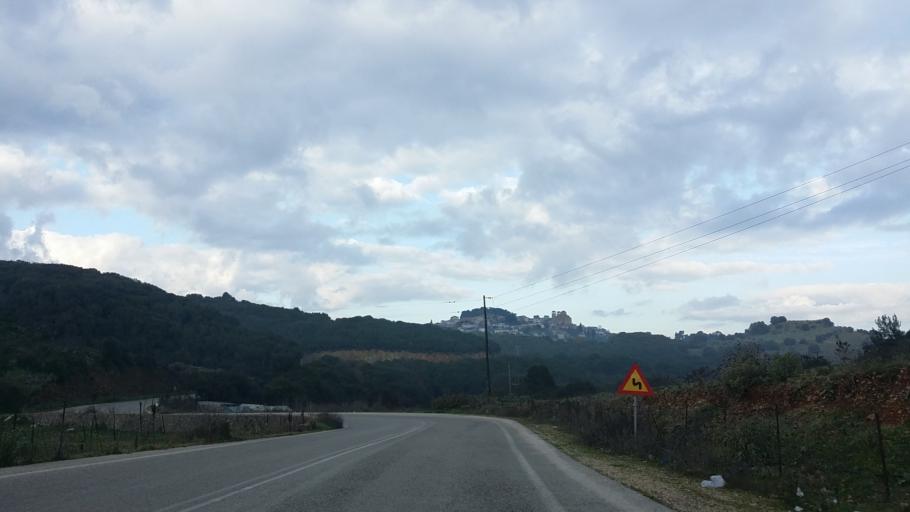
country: GR
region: West Greece
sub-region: Nomos Aitolias kai Akarnanias
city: Katouna
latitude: 38.7775
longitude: 21.1282
